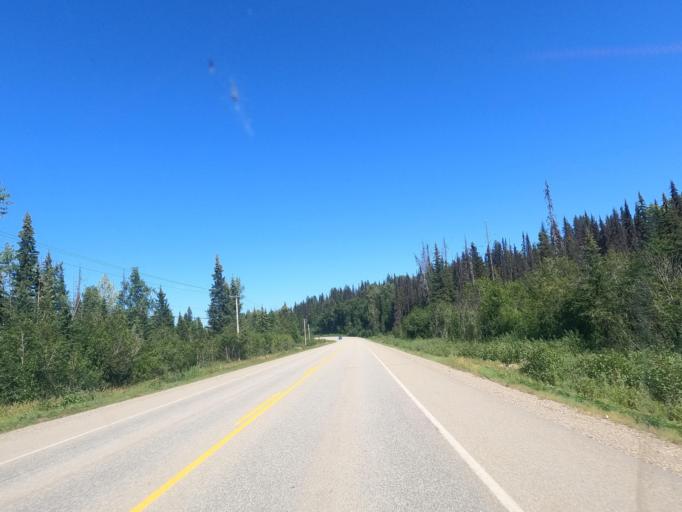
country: CA
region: British Columbia
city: Prince George
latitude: 54.3694
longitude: -122.6399
